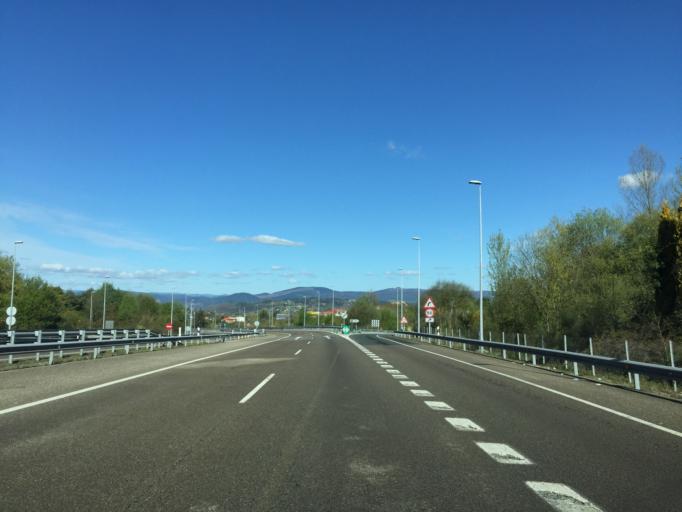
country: ES
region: Asturias
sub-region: Province of Asturias
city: Oviedo
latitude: 43.3461
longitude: -5.8935
